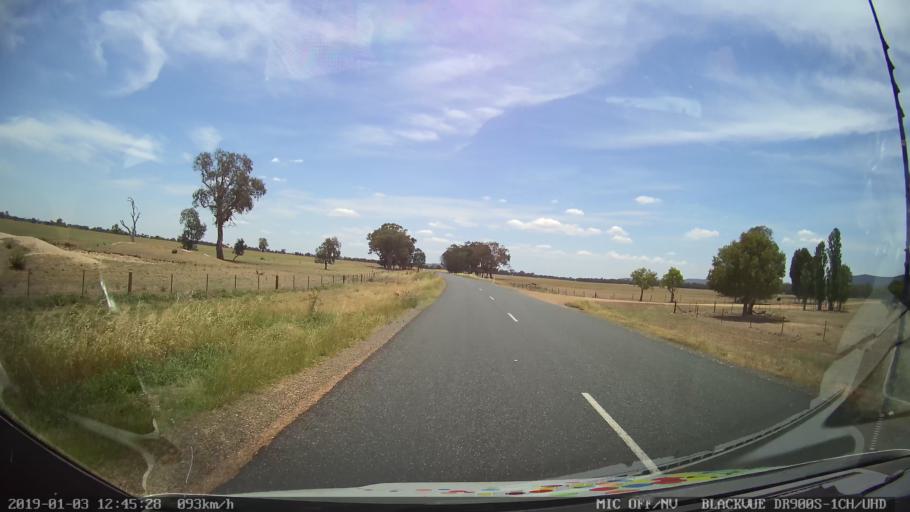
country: AU
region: New South Wales
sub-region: Weddin
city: Grenfell
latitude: -33.7492
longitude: 148.2237
